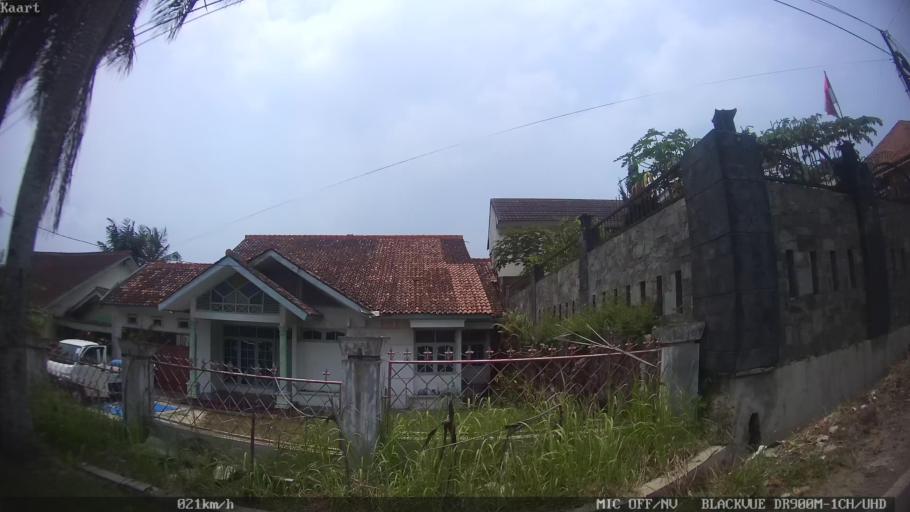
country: ID
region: Lampung
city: Bandarlampung
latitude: -5.4063
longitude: 105.2887
